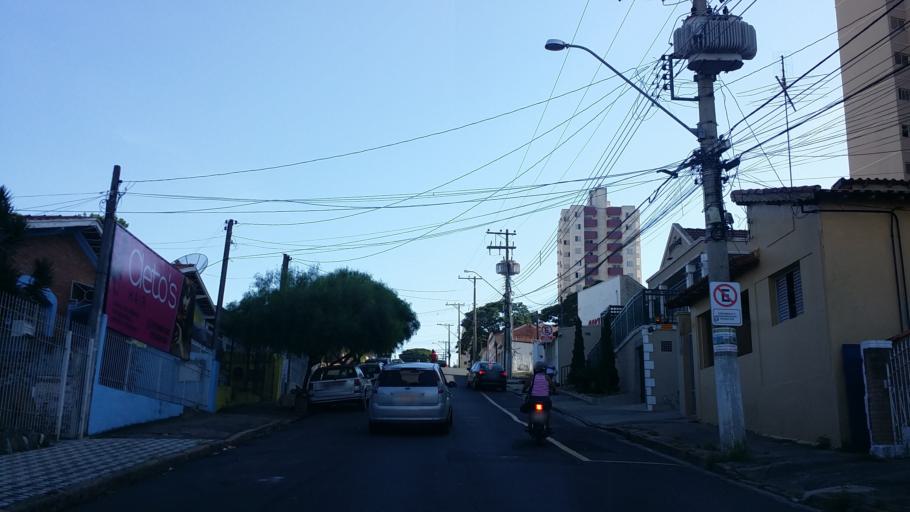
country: BR
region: Sao Paulo
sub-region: Indaiatuba
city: Indaiatuba
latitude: -23.0917
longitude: -47.2146
